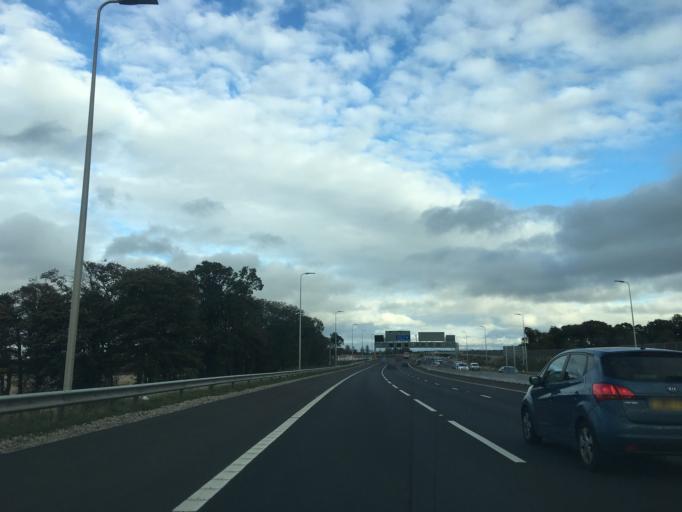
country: GB
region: Scotland
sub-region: Edinburgh
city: Queensferry
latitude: 55.9809
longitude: -3.4092
